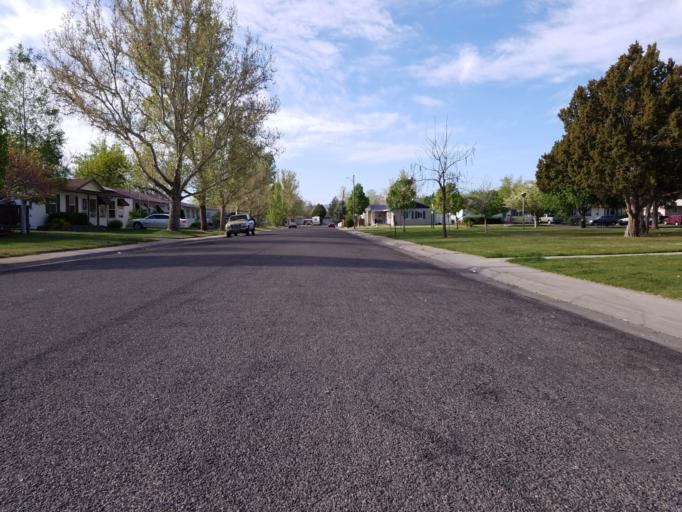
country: US
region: Colorado
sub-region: Mesa County
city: Grand Junction
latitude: 39.0844
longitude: -108.5345
